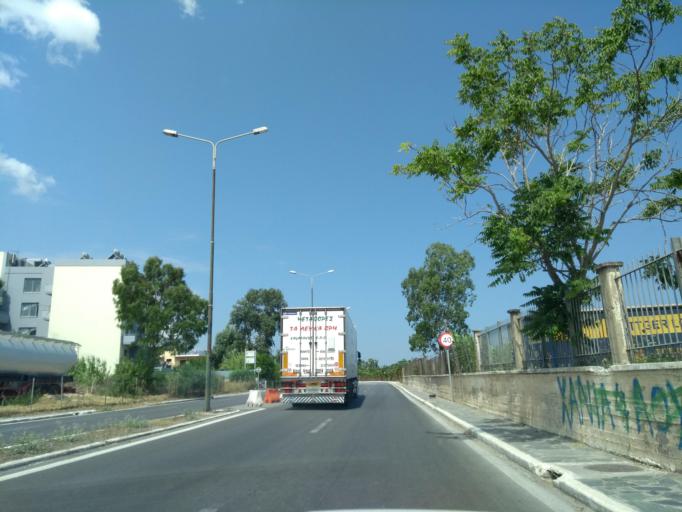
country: GR
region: Crete
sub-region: Nomos Chanias
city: Souda
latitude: 35.4889
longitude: 24.0709
